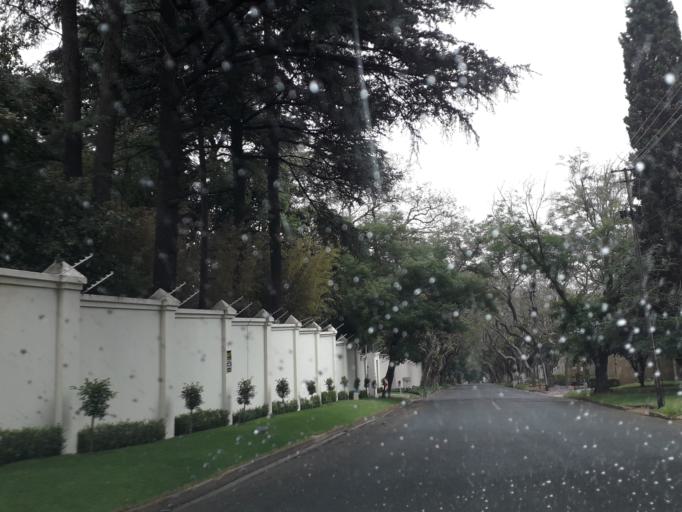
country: ZA
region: Gauteng
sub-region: City of Johannesburg Metropolitan Municipality
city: Johannesburg
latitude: -26.1345
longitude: 28.0389
